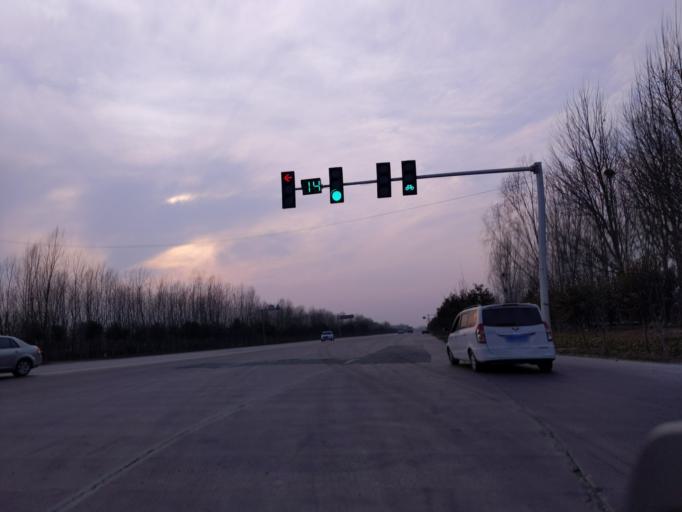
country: CN
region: Henan Sheng
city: Puyang
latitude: 35.8193
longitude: 114.9930
